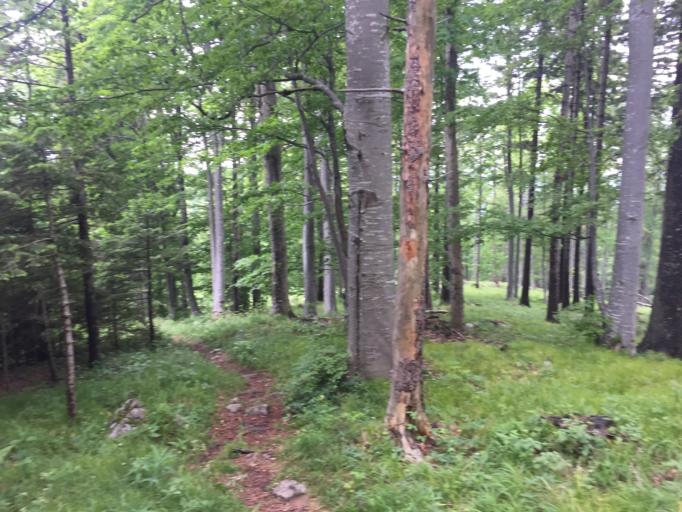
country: SI
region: Dobrna
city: Dobrna
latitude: 46.3903
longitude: 15.2396
